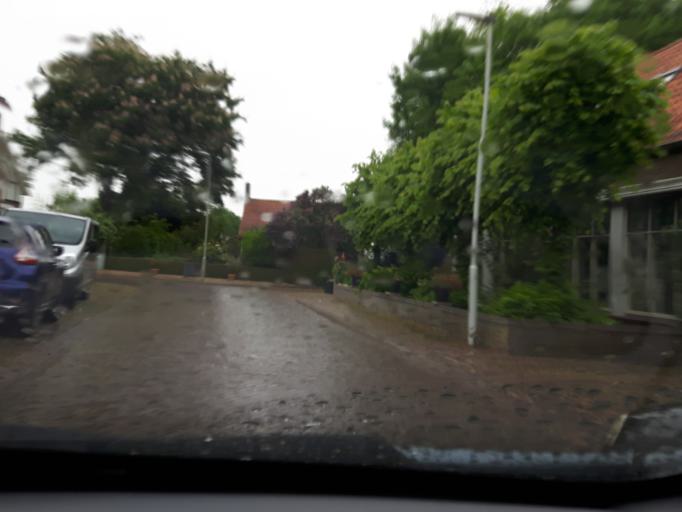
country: NL
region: Zeeland
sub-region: Gemeente Terneuzen
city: Terneuzen
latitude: 51.3899
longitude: 3.8161
